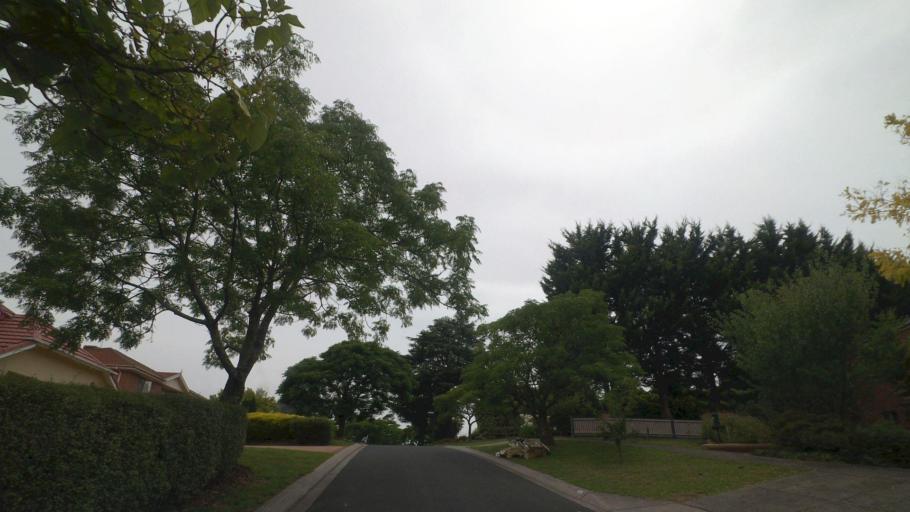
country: AU
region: Victoria
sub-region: Yarra Ranges
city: Kilsyth
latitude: -37.7851
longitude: 145.3370
